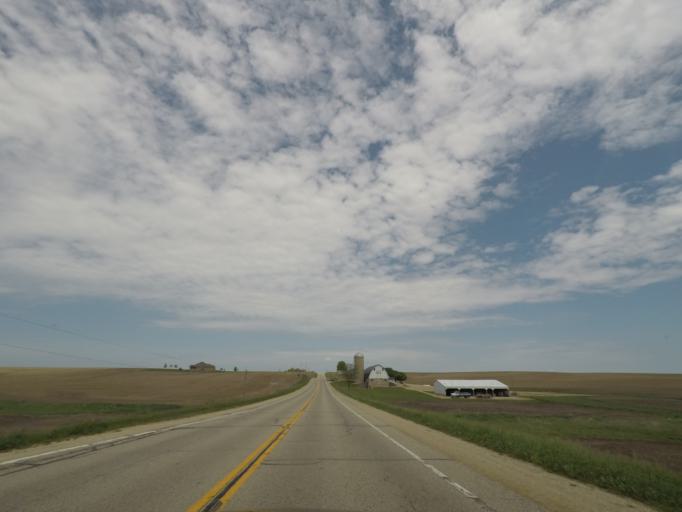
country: US
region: Wisconsin
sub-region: Rock County
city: Orfordville
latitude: 42.6876
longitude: -89.2882
